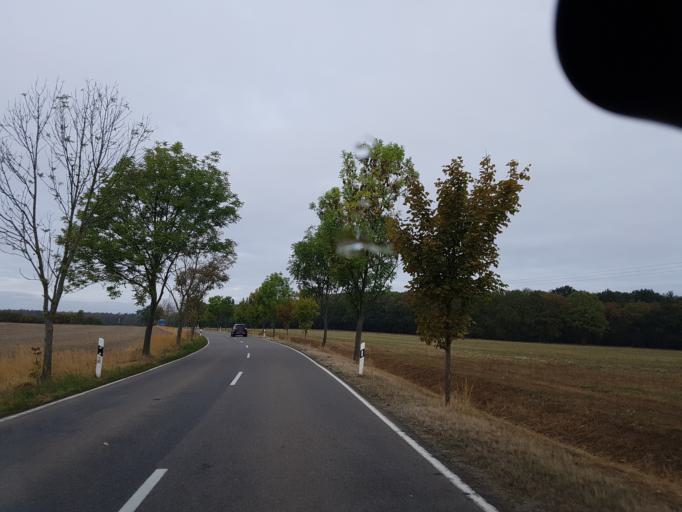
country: DE
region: Saxony-Anhalt
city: Klieken
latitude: 51.9291
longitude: 12.3745
